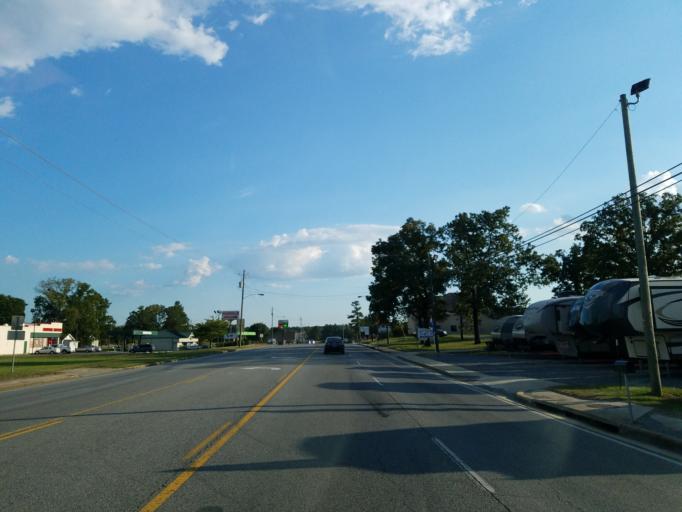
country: US
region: Georgia
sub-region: Murray County
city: Chatsworth
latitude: 34.7602
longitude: -84.7695
